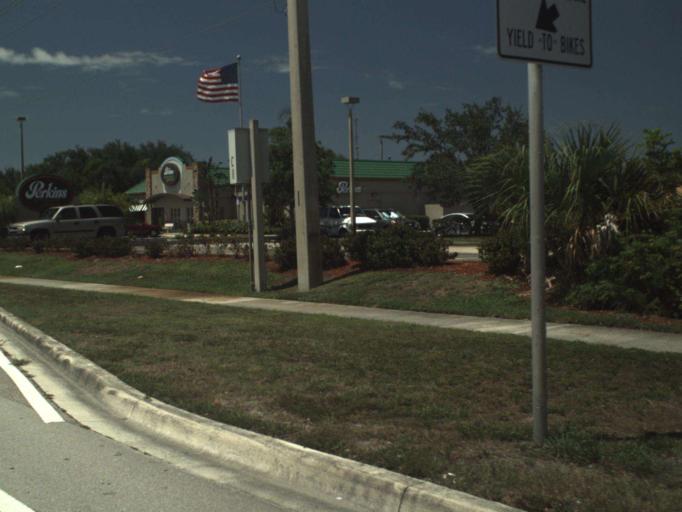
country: US
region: Florida
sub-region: Saint Lucie County
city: River Park
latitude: 27.2991
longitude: -80.3046
